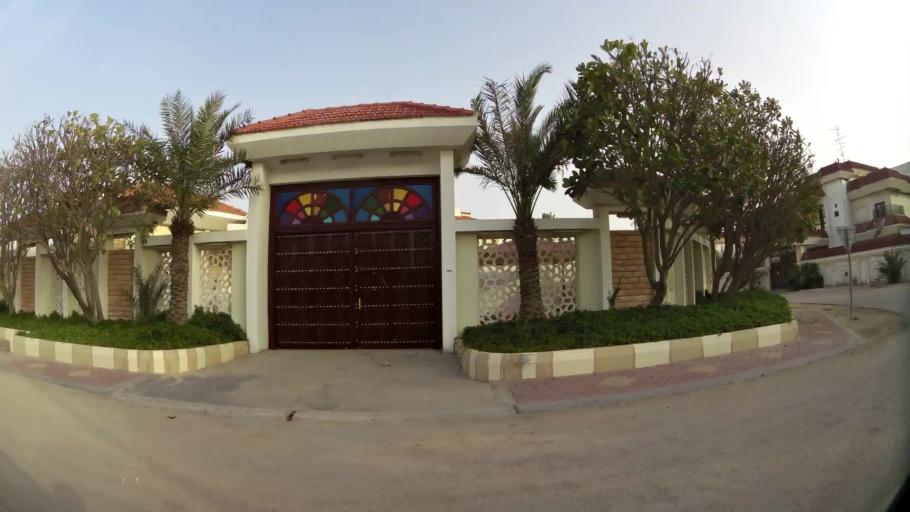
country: QA
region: Baladiyat ar Rayyan
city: Ar Rayyan
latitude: 25.2403
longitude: 51.4521
